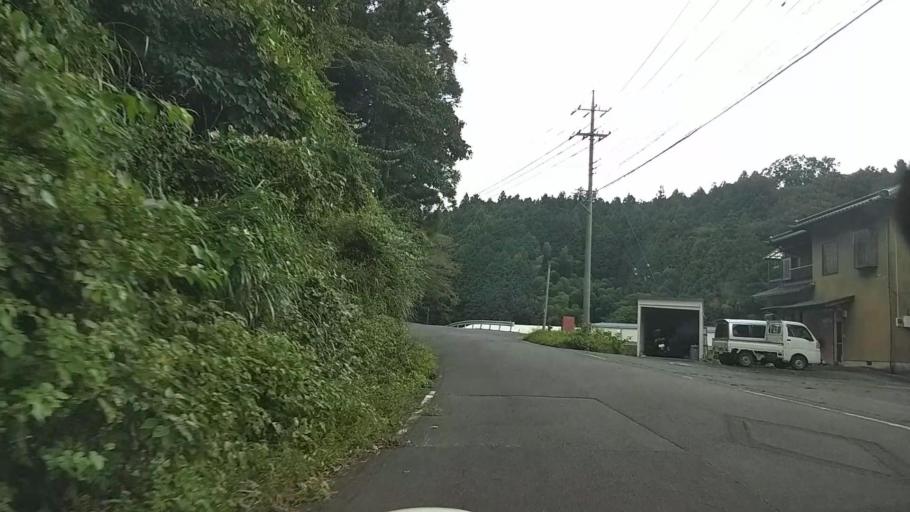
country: JP
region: Shizuoka
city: Fujinomiya
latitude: 35.2166
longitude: 138.5172
